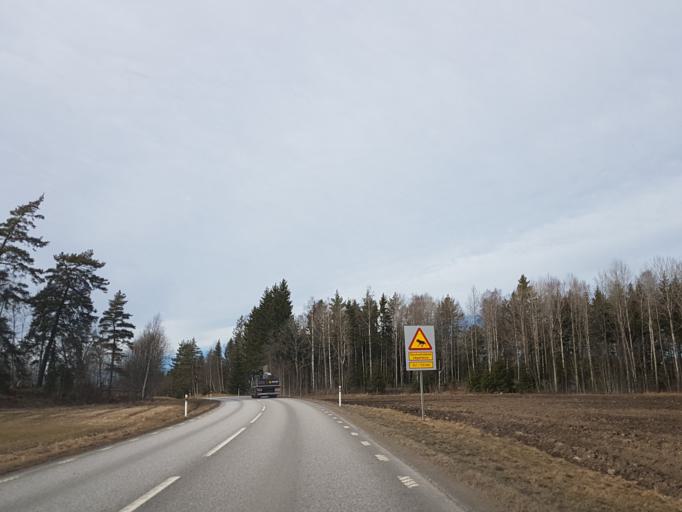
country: SE
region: Stockholm
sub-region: Norrtalje Kommun
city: Norrtalje
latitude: 59.6831
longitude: 18.6815
